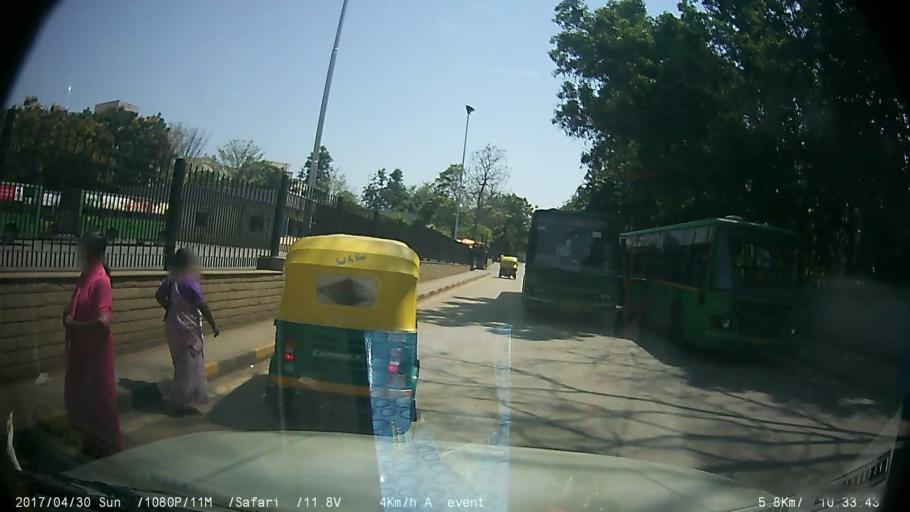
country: IN
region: Karnataka
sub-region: Bangalore Urban
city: Anekal
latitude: 12.8356
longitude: 77.6572
